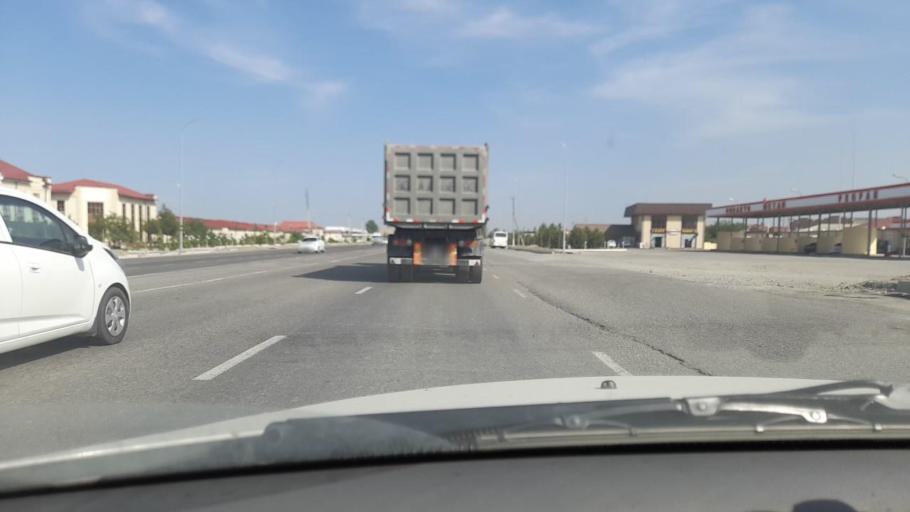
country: UZ
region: Samarqand
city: Daxbet
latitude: 39.7305
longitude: 66.9384
